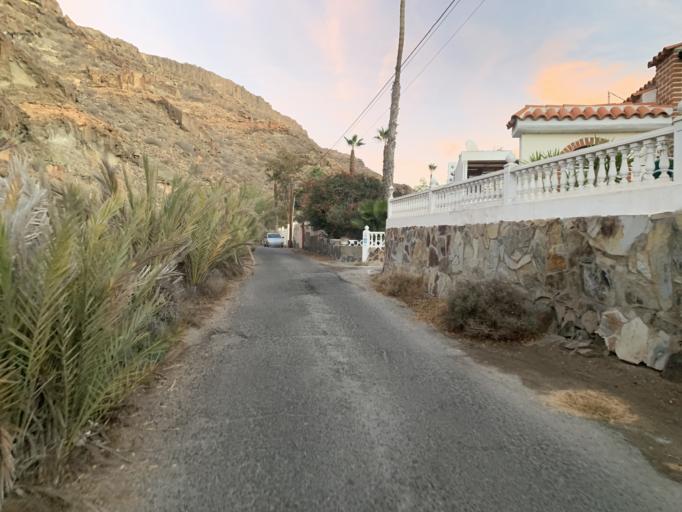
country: ES
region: Canary Islands
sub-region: Provincia de Las Palmas
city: Puerto Rico
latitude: 27.8073
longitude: -15.7303
